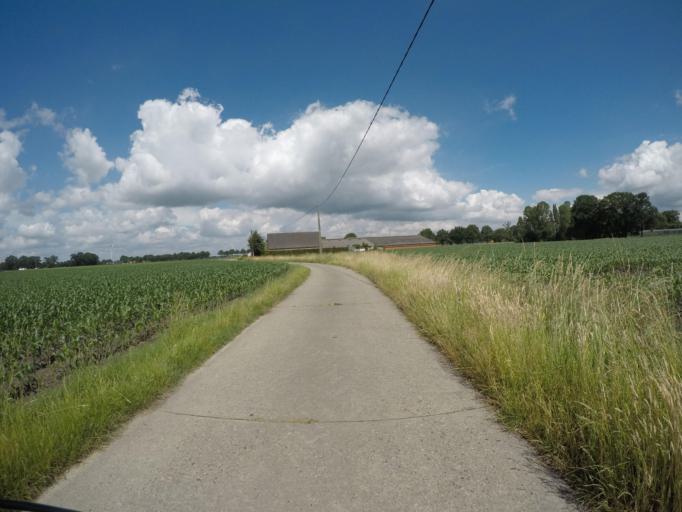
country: BE
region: Flanders
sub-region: Provincie Antwerpen
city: Brecht
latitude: 51.3553
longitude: 4.6800
